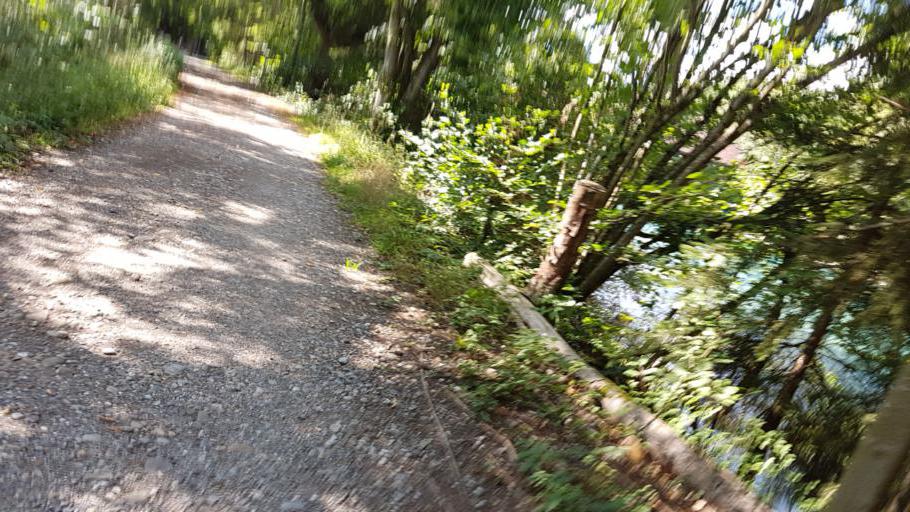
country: CH
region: Bern
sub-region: Bern-Mittelland District
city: Muri
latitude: 46.9182
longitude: 7.5011
